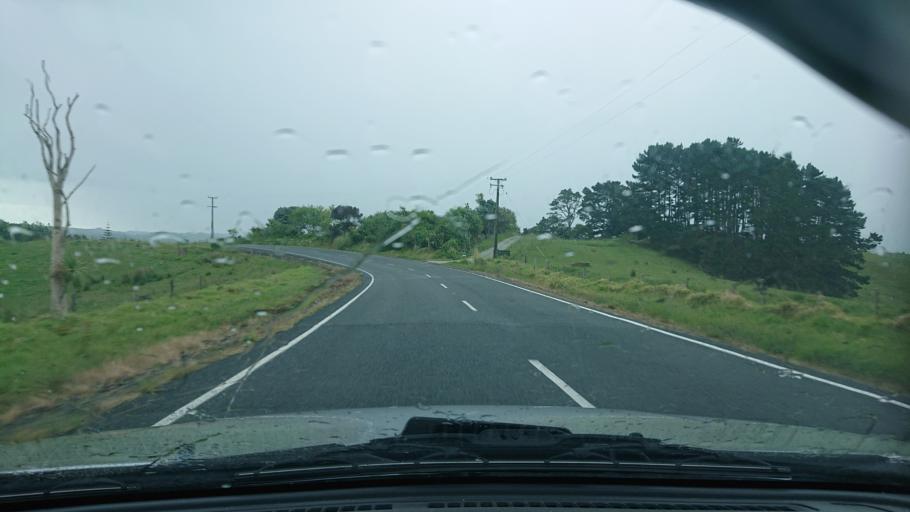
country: NZ
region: Auckland
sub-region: Auckland
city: Wellsford
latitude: -36.3344
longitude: 174.3945
